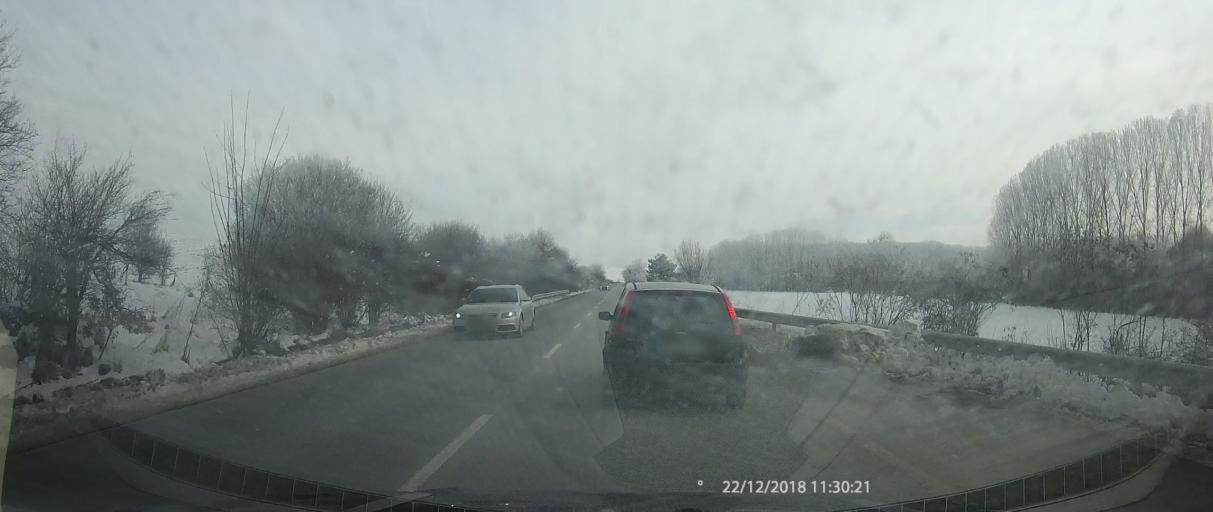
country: BG
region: Kyustendil
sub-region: Obshtina Bobovdol
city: Bobovdol
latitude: 42.2729
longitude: 22.9702
